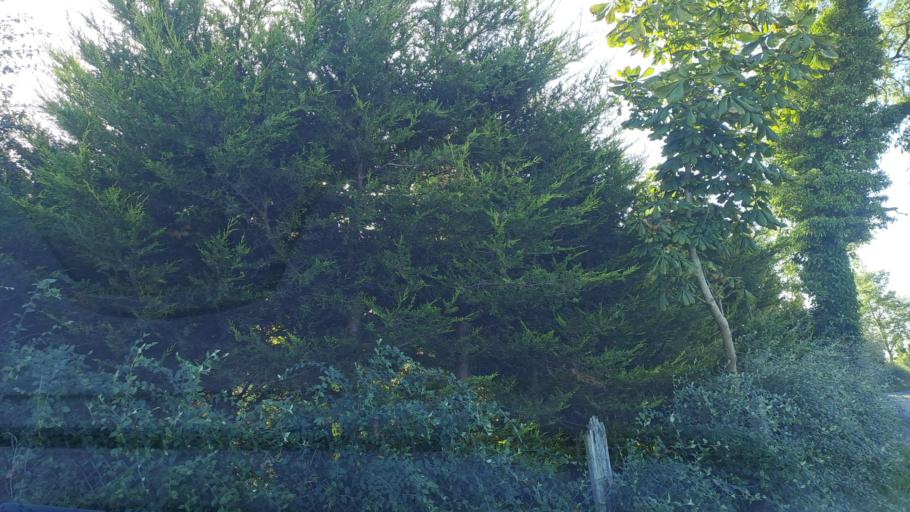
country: IE
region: Ulster
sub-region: An Cabhan
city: Kingscourt
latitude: 53.9841
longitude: -6.8609
